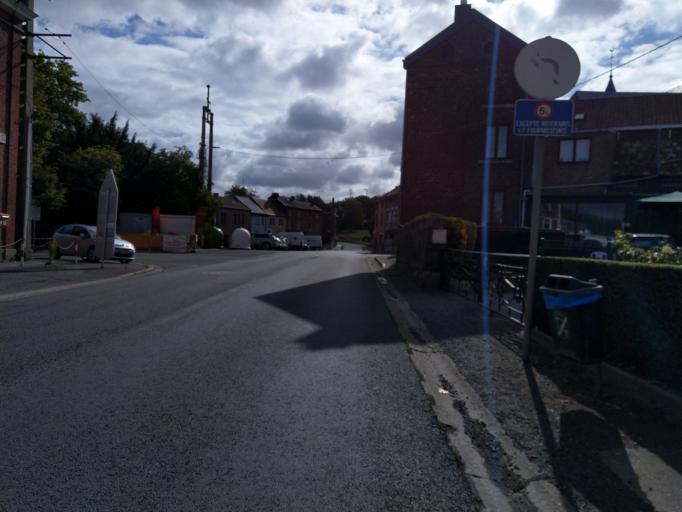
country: BE
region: Wallonia
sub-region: Province de Liege
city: Flemalle-Haute
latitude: 50.5837
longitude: 5.4432
